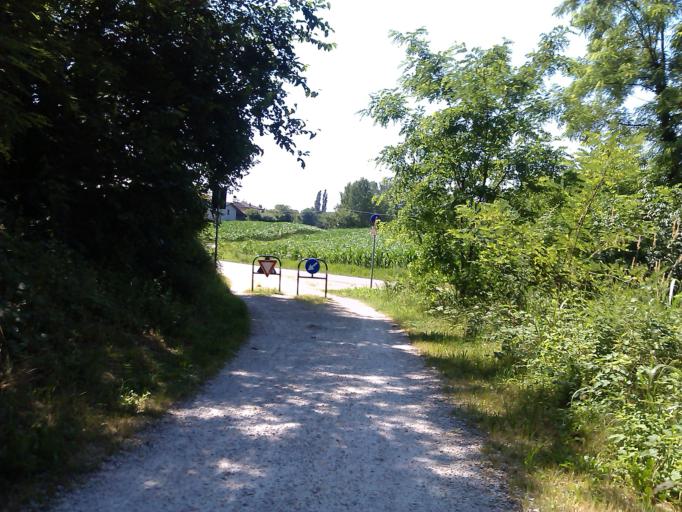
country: IT
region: Veneto
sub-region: Provincia di Treviso
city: Loria Bessica
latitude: 45.7256
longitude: 11.8740
